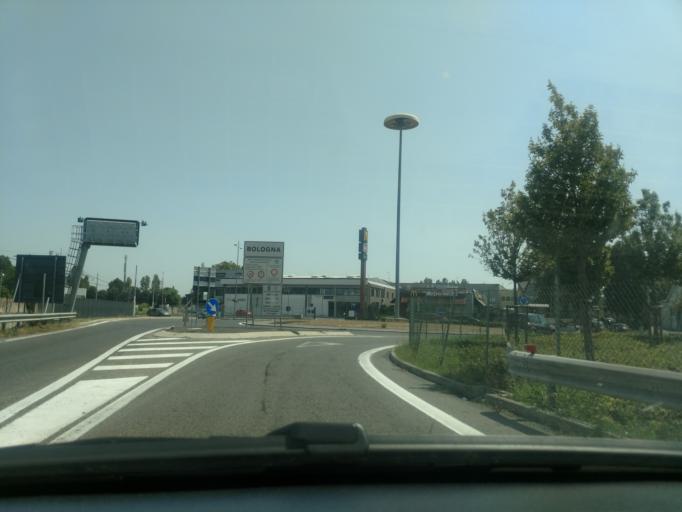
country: IT
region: Emilia-Romagna
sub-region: Provincia di Bologna
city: San Lazzaro
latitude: 44.4965
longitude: 11.3920
